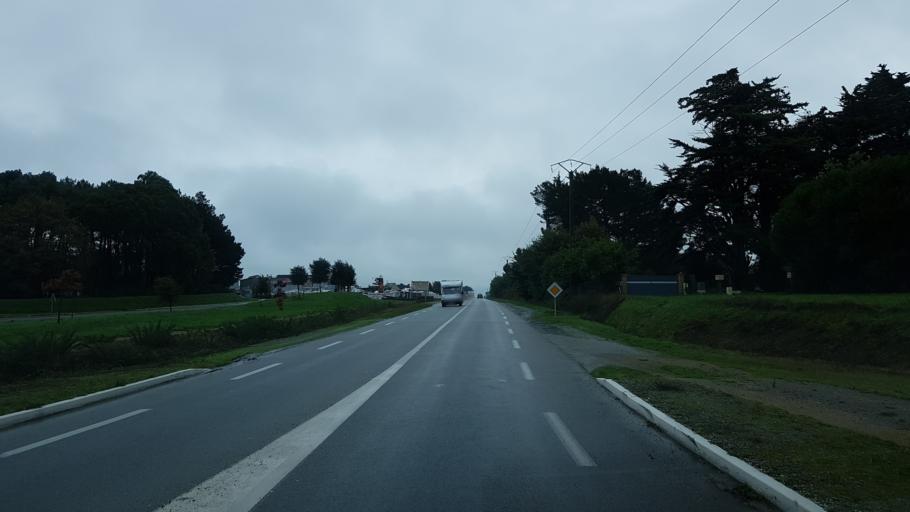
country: FR
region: Brittany
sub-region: Departement du Morbihan
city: Sarzeau
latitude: 47.5265
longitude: -2.7939
